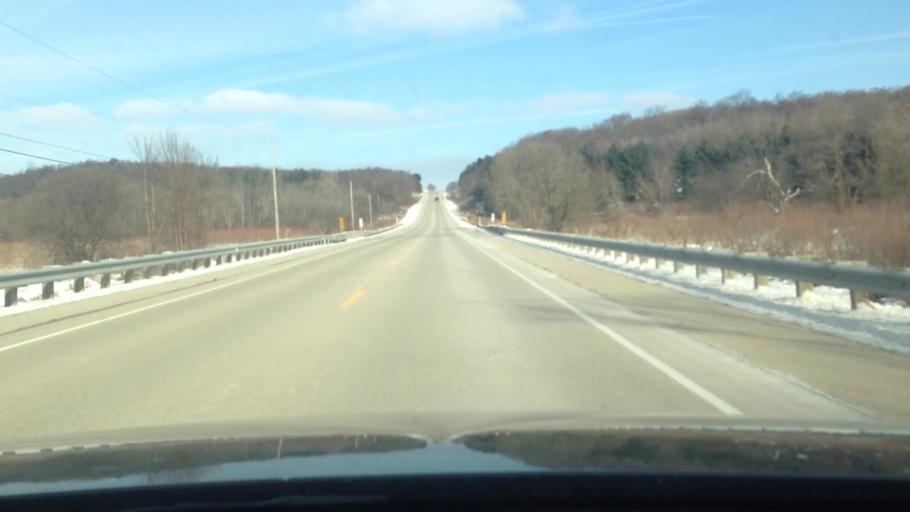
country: US
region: Wisconsin
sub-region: Walworth County
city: East Troy
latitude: 42.7311
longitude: -88.4057
